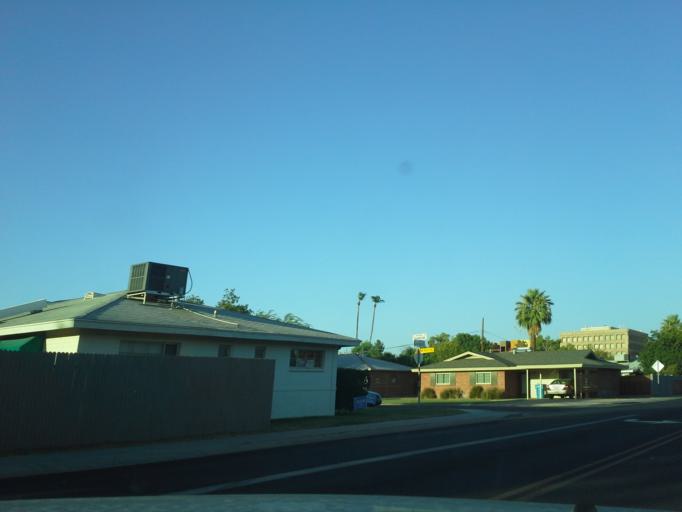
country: US
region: Arizona
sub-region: Maricopa County
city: Phoenix
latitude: 33.5020
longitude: -112.0780
